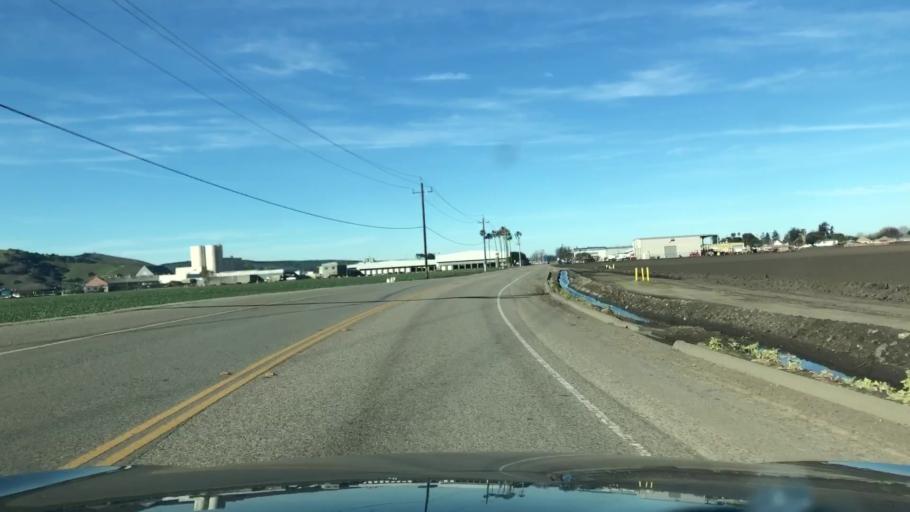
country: US
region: California
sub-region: Monterey County
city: Salinas
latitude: 36.6190
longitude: -121.6386
